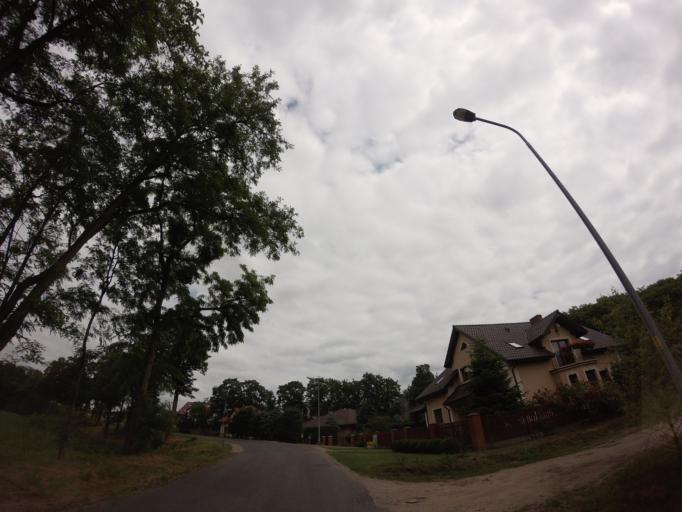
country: PL
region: Lubusz
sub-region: Powiat strzelecko-drezdenecki
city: Strzelce Krajenskie
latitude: 52.8762
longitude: 15.5435
